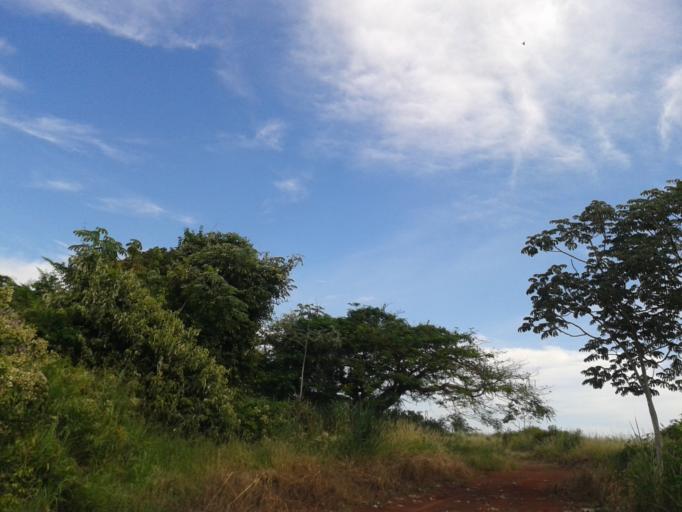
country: BR
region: Minas Gerais
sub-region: Capinopolis
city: Capinopolis
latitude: -18.6494
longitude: -49.6980
